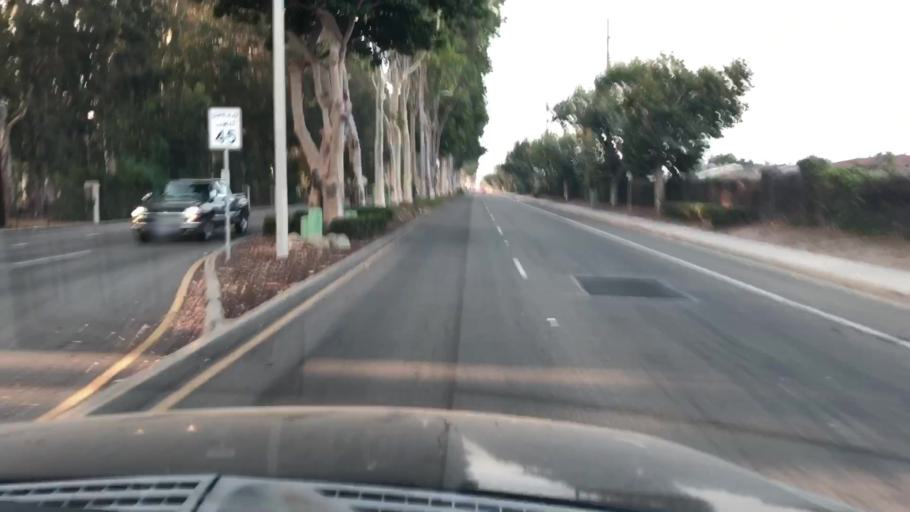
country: US
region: California
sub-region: Ventura County
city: Port Hueneme
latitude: 34.1569
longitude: -119.1951
